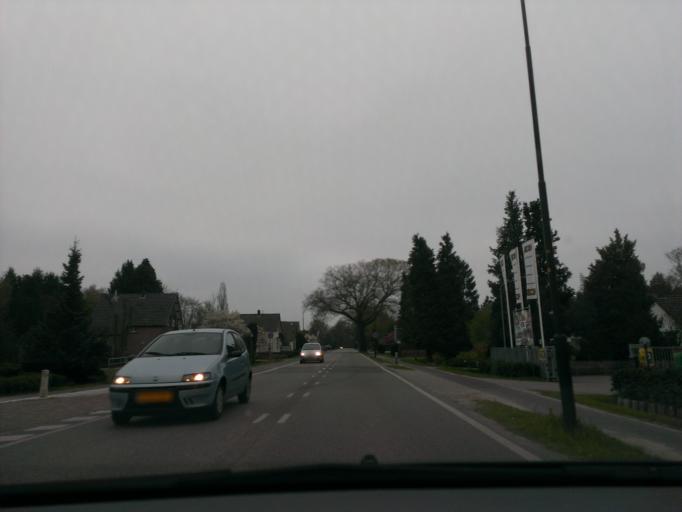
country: NL
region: Gelderland
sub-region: Gemeente Apeldoorn
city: Apeldoorn
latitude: 52.2445
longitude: 5.9554
